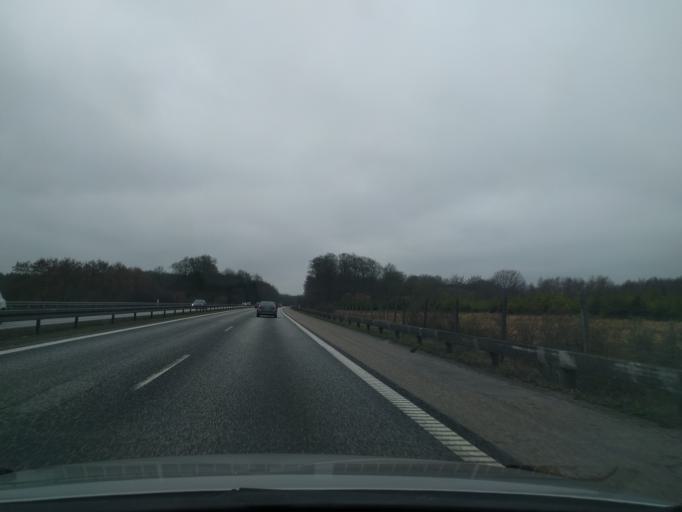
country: DK
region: Zealand
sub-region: Soro Kommune
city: Soro
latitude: 55.4422
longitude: 11.5063
